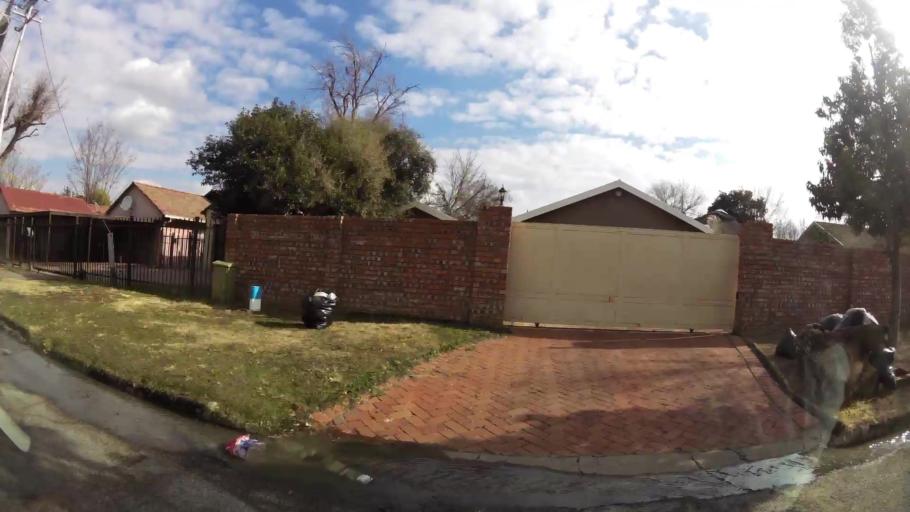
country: ZA
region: Orange Free State
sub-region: Mangaung Metropolitan Municipality
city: Bloemfontein
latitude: -29.0876
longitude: 26.2511
